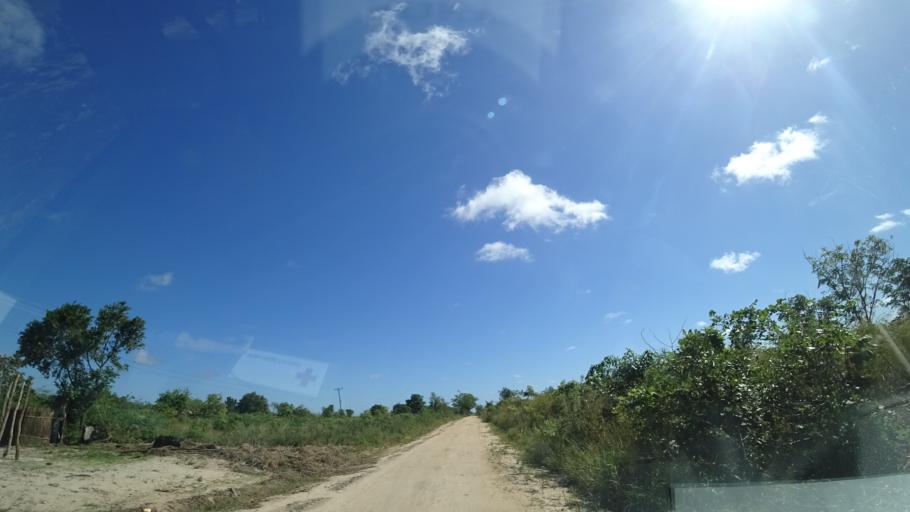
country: MZ
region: Sofala
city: Dondo
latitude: -19.2864
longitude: 34.6868
